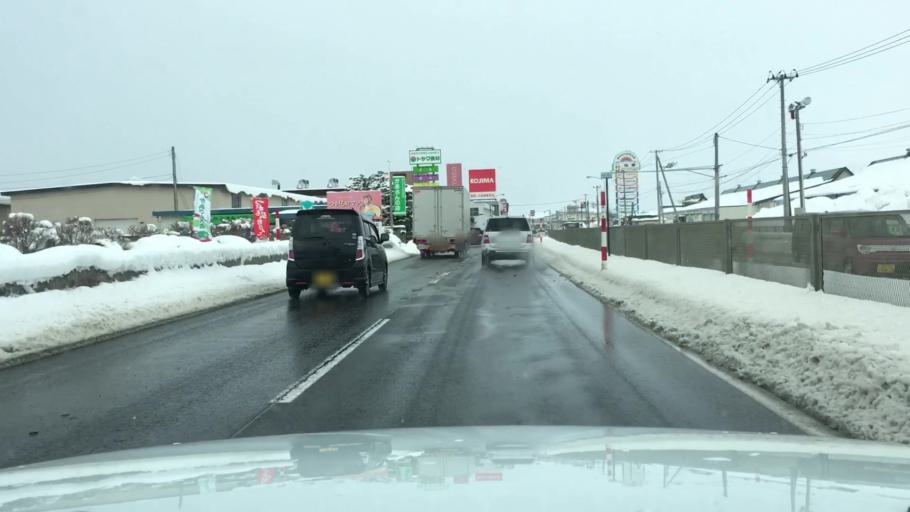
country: JP
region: Aomori
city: Hirosaki
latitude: 40.6048
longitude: 140.4991
